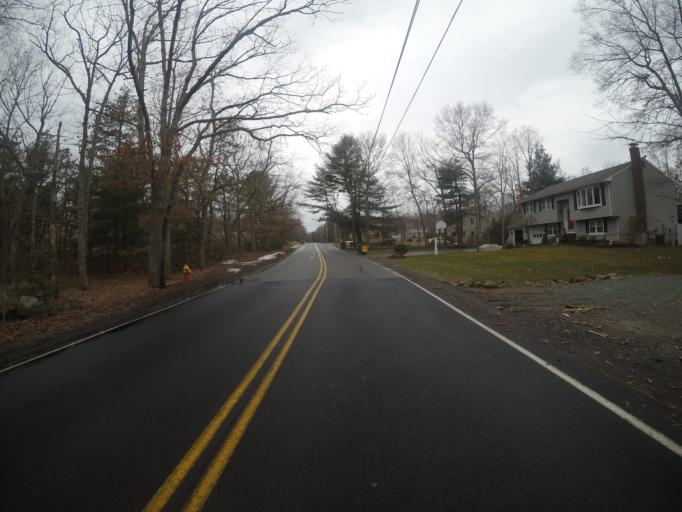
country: US
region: Massachusetts
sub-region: Bristol County
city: Easton
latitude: 42.0483
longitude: -71.1659
